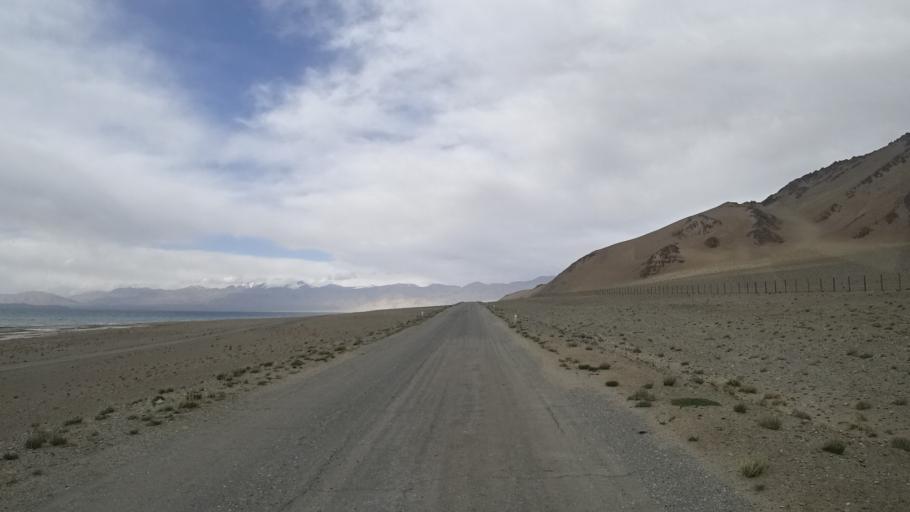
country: TJ
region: Gorno-Badakhshan
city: Murghob
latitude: 38.9700
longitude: 73.5361
